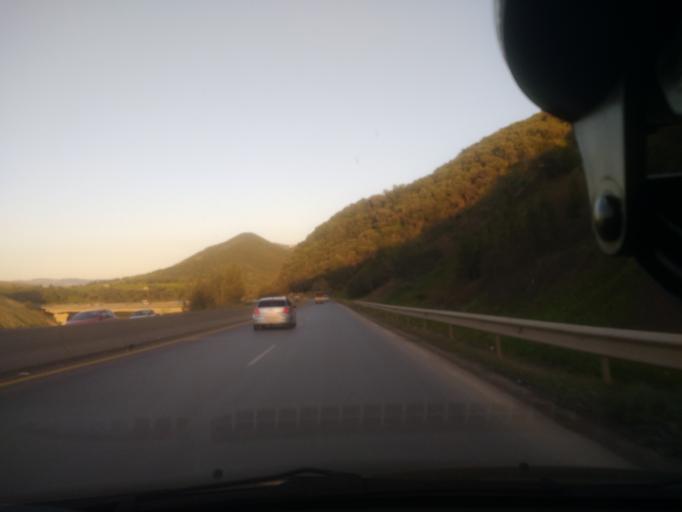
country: DZ
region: Tizi Ouzou
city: Tizi Ouzou
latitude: 36.7486
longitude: 4.0256
